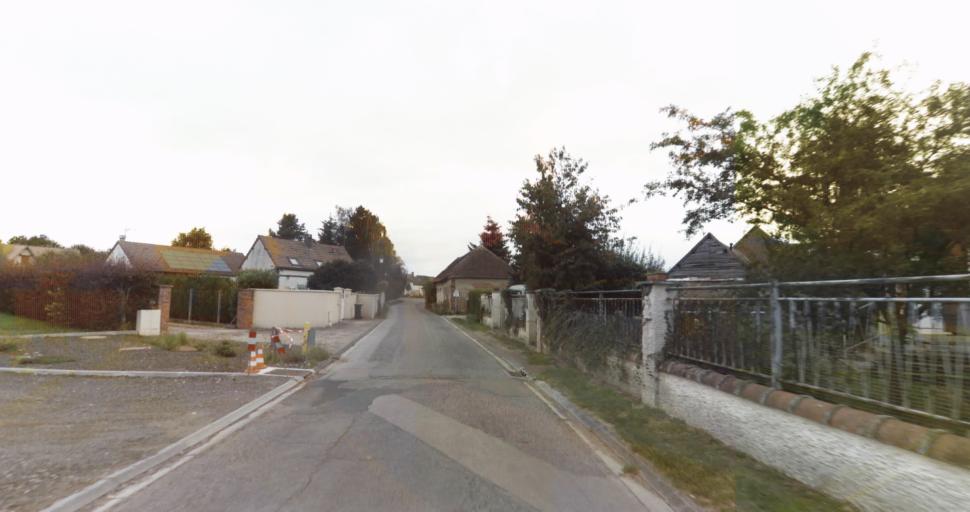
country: FR
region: Centre
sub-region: Departement d'Eure-et-Loir
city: Sorel-Moussel
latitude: 48.8627
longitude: 1.3477
